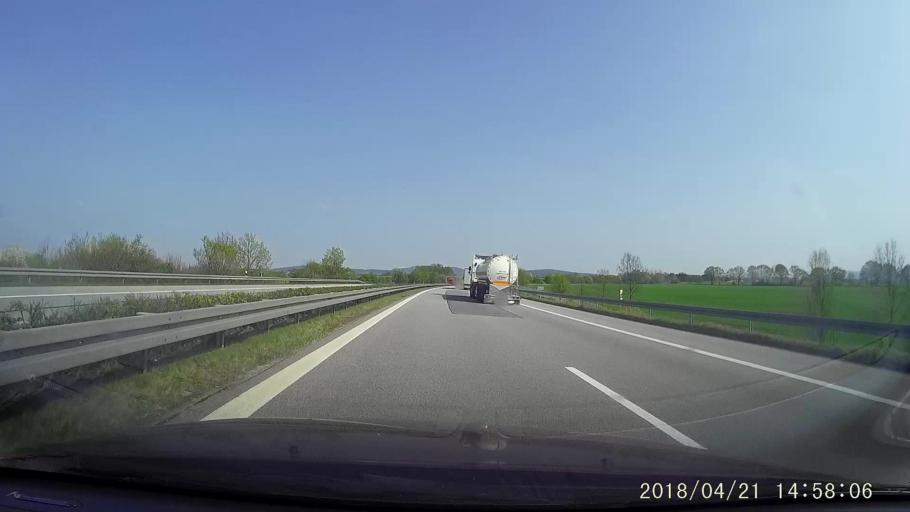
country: DE
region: Saxony
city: Weissenberg
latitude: 51.2123
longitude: 14.7251
